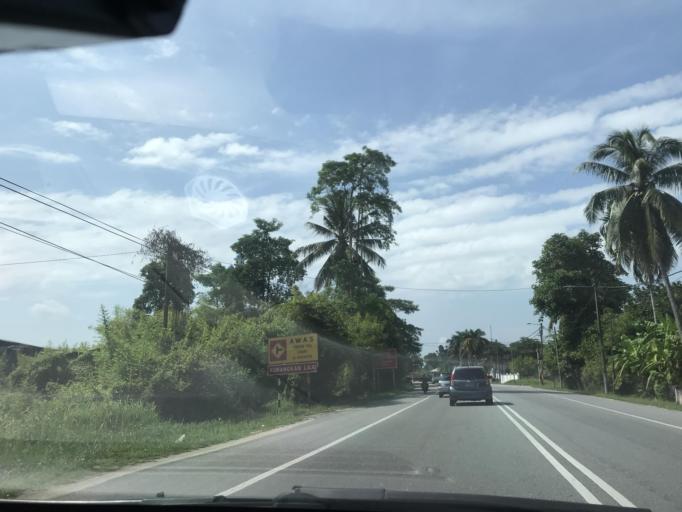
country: MY
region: Kelantan
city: Kota Bharu
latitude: 6.1340
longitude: 102.1750
